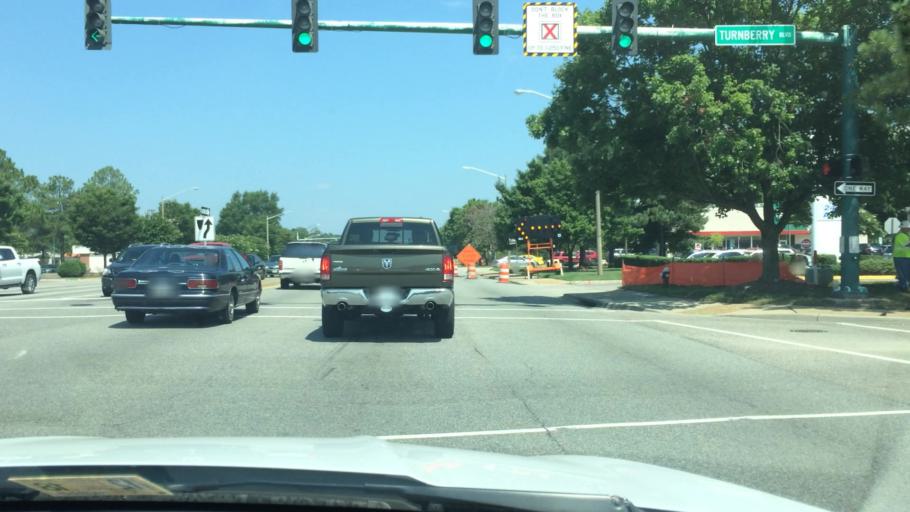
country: US
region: Virginia
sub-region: York County
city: Yorktown
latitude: 37.1350
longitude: -76.5172
